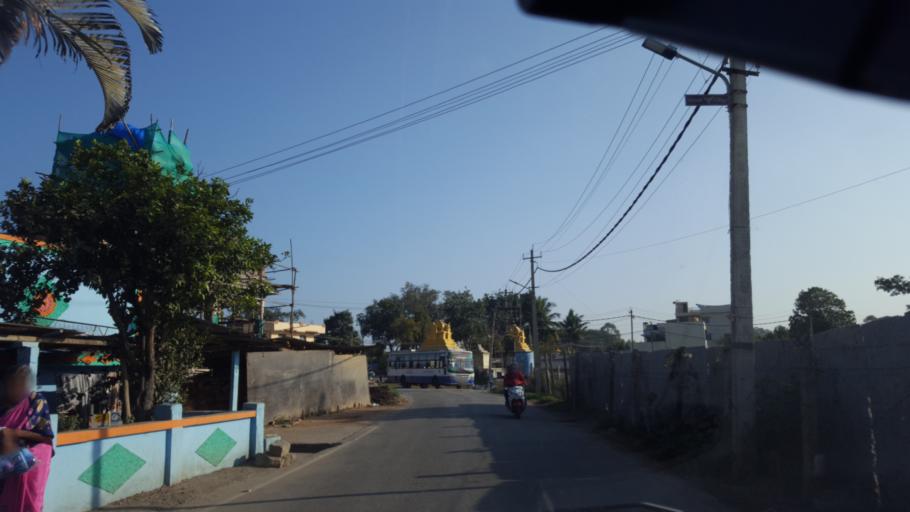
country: IN
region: Karnataka
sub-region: Bangalore Rural
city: Hoskote
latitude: 12.9159
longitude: 77.7654
